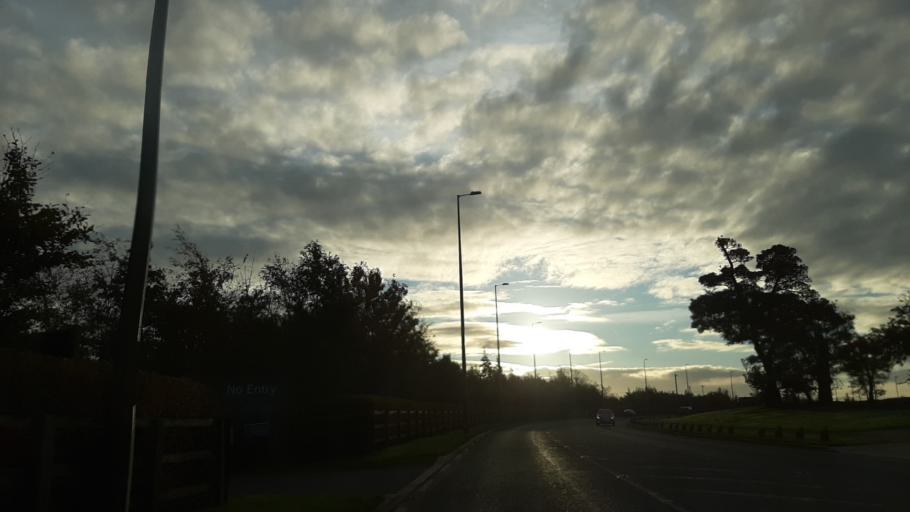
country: IE
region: Leinster
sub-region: Kildare
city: Athgarvan
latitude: 53.1698
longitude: -6.8419
